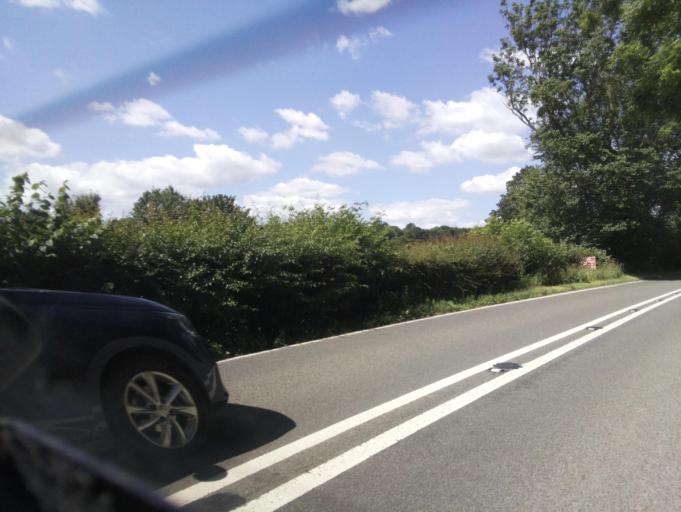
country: GB
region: England
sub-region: Derbyshire
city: Ashbourne
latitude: 53.0317
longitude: -1.7363
